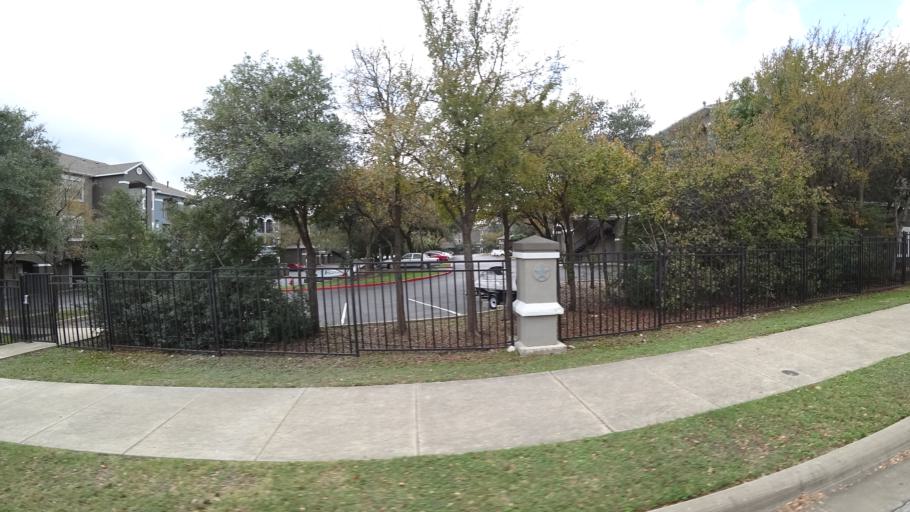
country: US
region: Texas
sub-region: Williamson County
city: Anderson Mill
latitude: 30.4157
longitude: -97.8452
